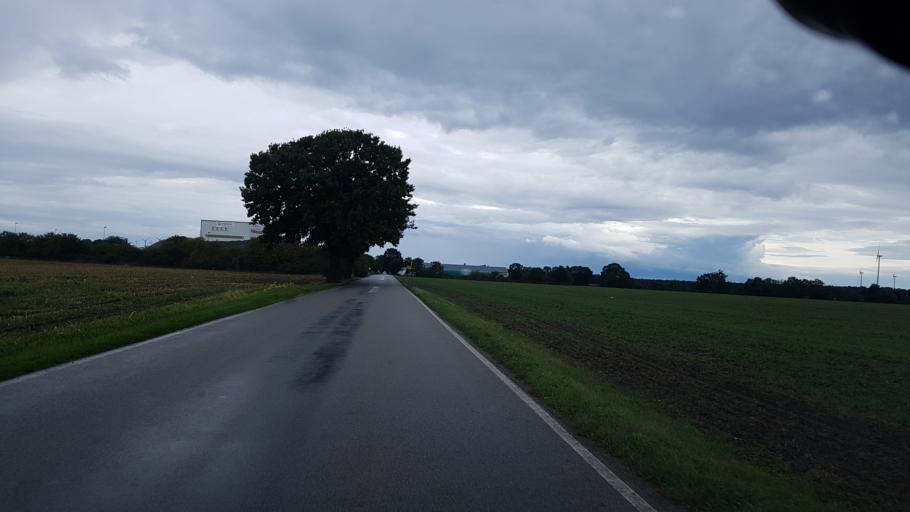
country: DE
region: Brandenburg
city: Grossraschen
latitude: 51.5793
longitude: 14.0421
